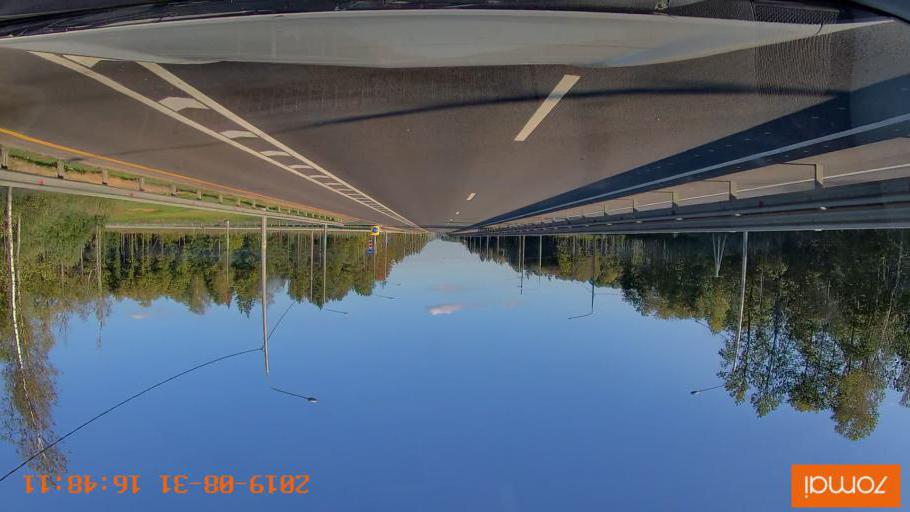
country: RU
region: Kaluga
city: Pyatovskiy
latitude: 54.6676
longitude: 36.1448
